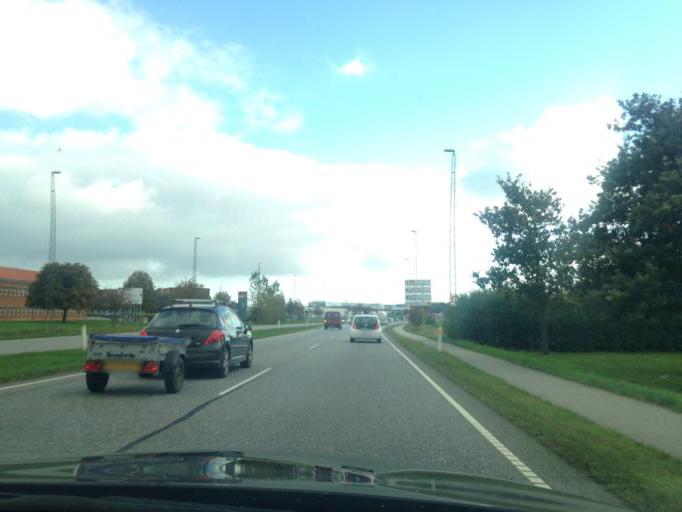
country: DK
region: South Denmark
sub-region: Vejle Kommune
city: Vejle
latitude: 55.6769
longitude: 9.5775
